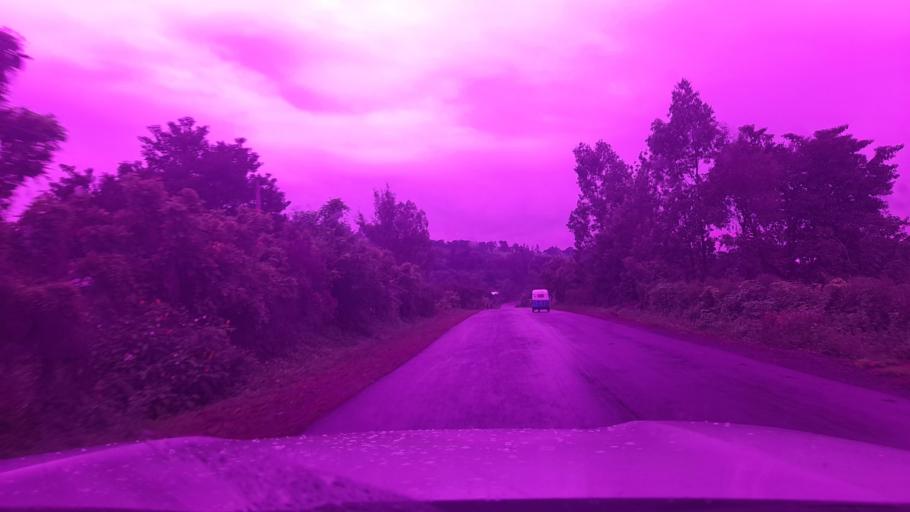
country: ET
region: Oromiya
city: Jima
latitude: 7.8068
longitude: 37.3441
